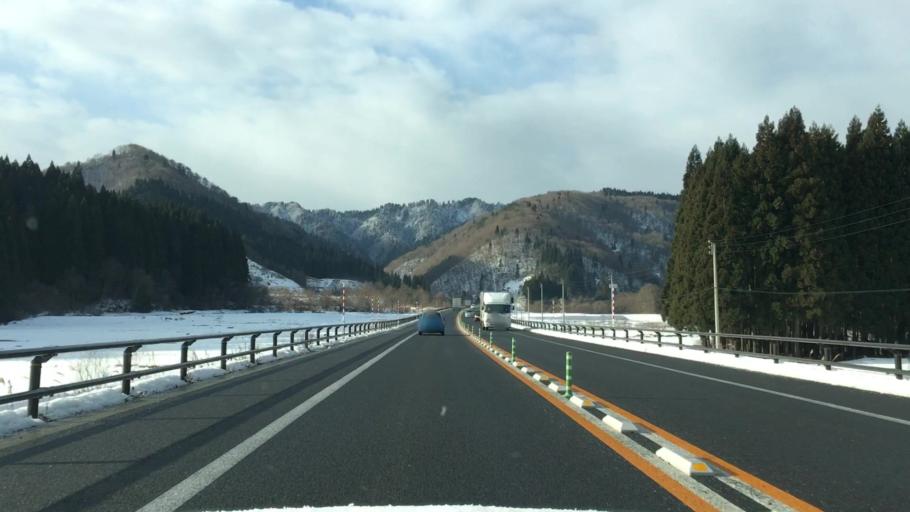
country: JP
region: Akita
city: Odate
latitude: 40.2345
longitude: 140.4974
